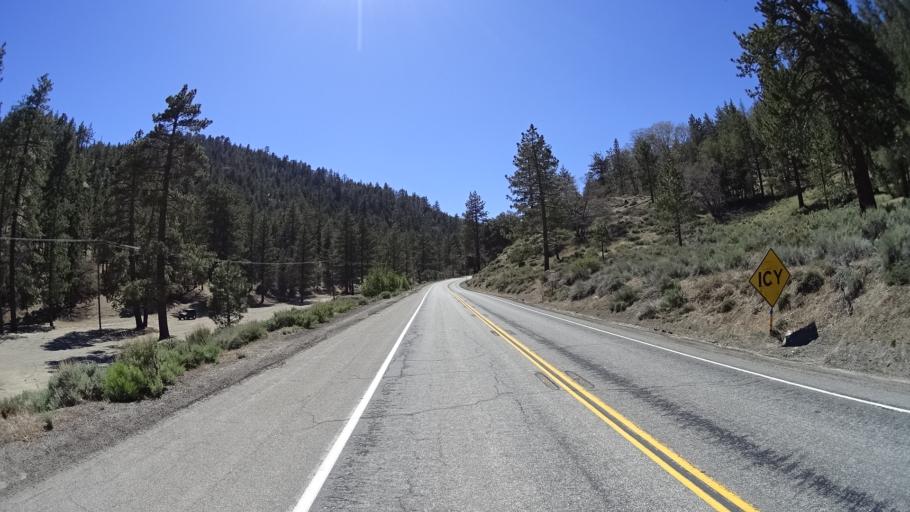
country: US
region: California
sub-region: San Bernardino County
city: Wrightwood
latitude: 34.3744
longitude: -117.6812
